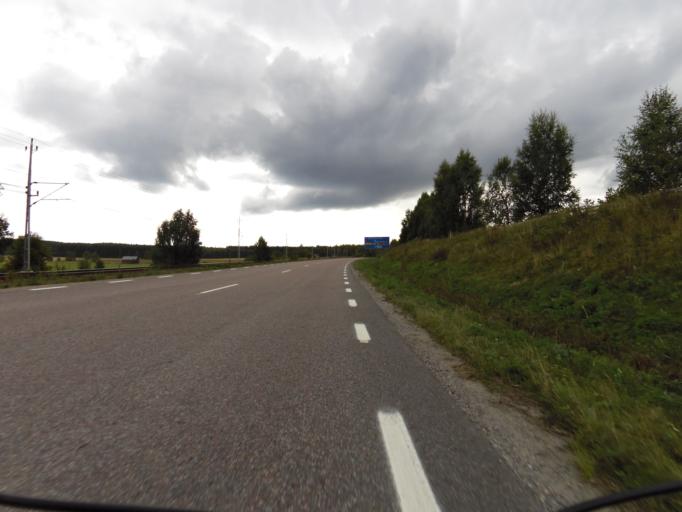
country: SE
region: Gaevleborg
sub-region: Ockelbo Kommun
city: Ockelbo
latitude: 60.8820
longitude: 16.7157
